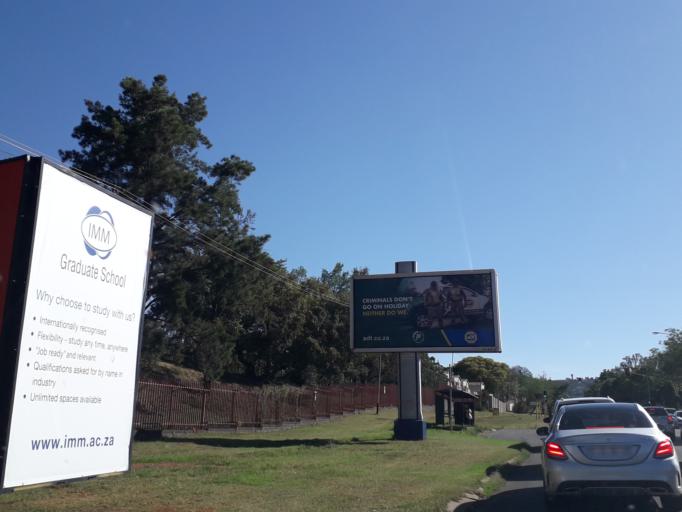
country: ZA
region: Gauteng
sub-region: City of Johannesburg Metropolitan Municipality
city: Roodepoort
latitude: -26.1387
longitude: 27.9587
